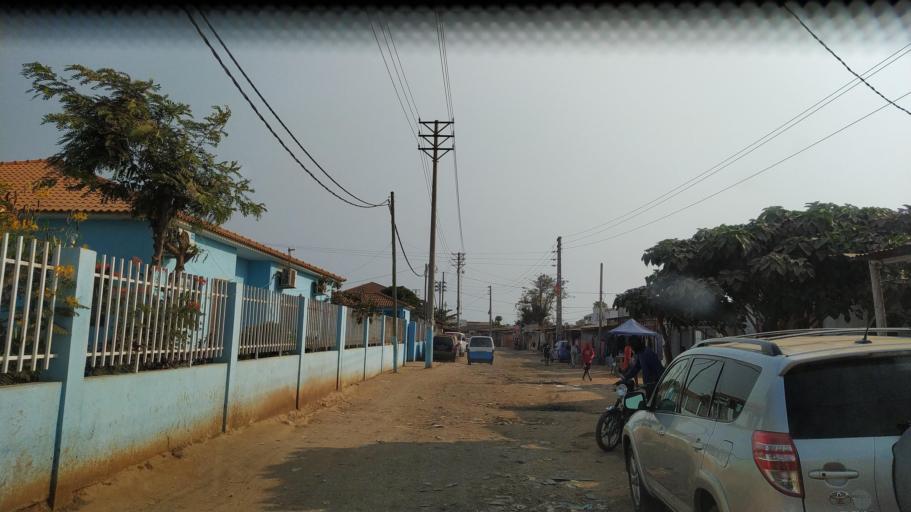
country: AO
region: Luanda
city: Luanda
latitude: -8.8673
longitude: 13.2020
